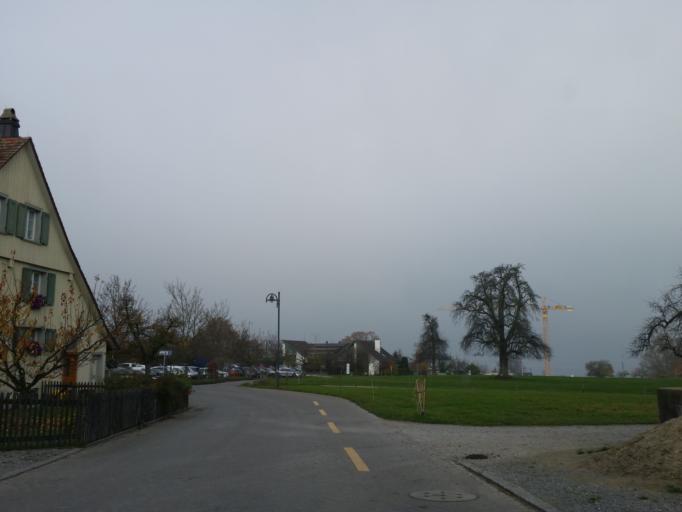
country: CH
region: Thurgau
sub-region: Arbon District
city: Egnach
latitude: 47.5342
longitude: 9.3989
